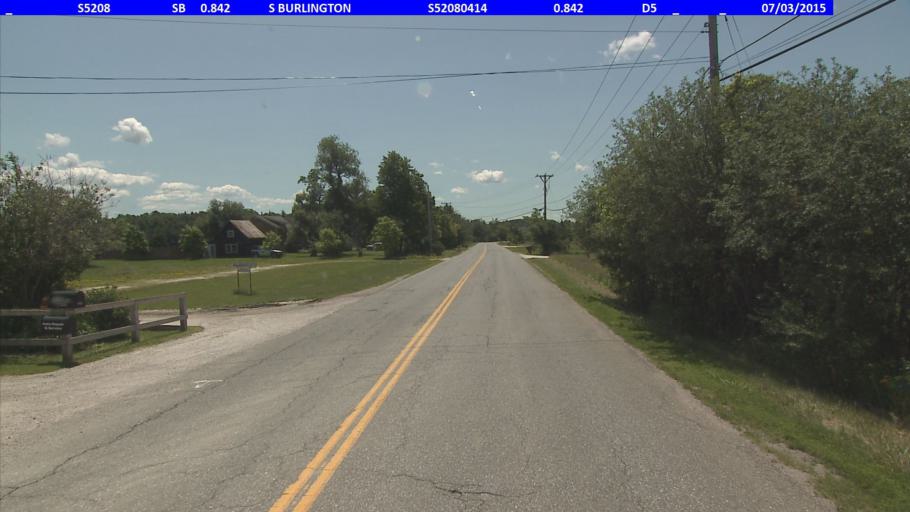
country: US
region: Vermont
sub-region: Chittenden County
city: South Burlington
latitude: 44.4230
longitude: -73.1736
